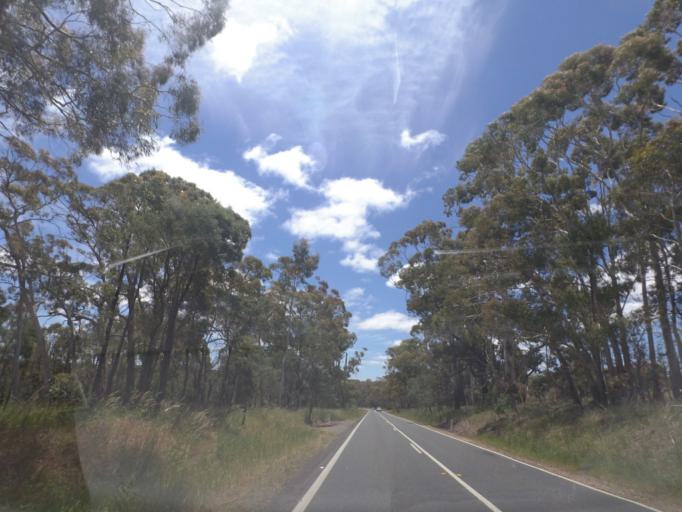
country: AU
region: Victoria
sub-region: Mount Alexander
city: Castlemaine
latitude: -37.3177
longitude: 144.1648
